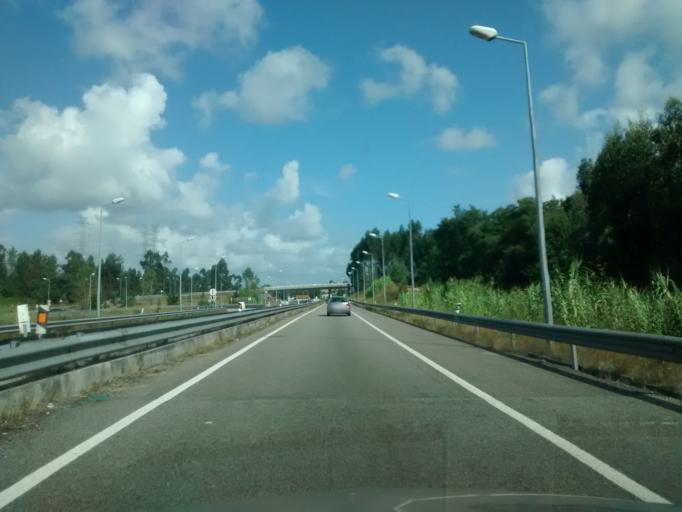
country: PT
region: Aveiro
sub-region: Anadia
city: Sangalhos
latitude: 40.4642
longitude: -8.4621
